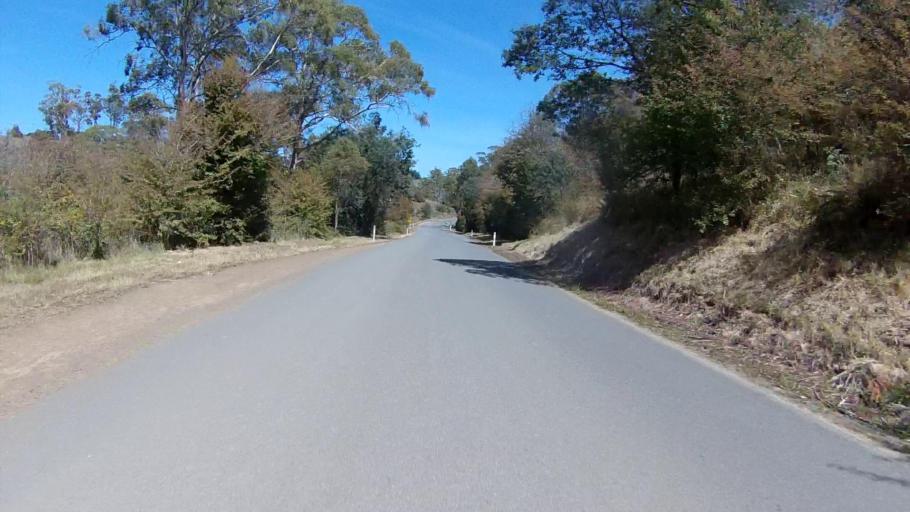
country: AU
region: Tasmania
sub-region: Sorell
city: Sorell
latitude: -42.7585
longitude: 147.6564
